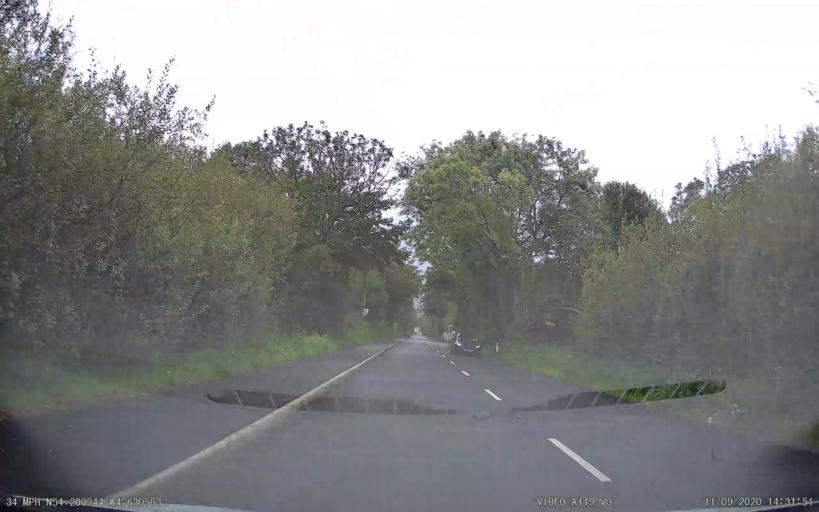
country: IM
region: Castletown
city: Castletown
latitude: 54.2009
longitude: -4.6306
